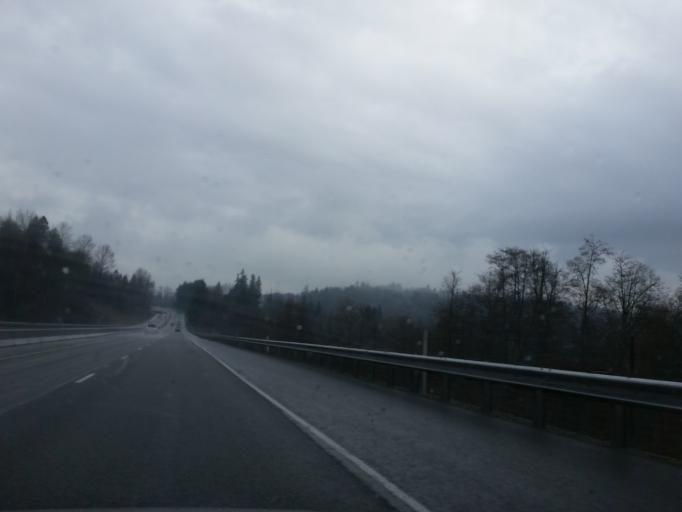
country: US
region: Washington
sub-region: Snohomish County
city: Monroe
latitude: 47.8304
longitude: -122.0283
